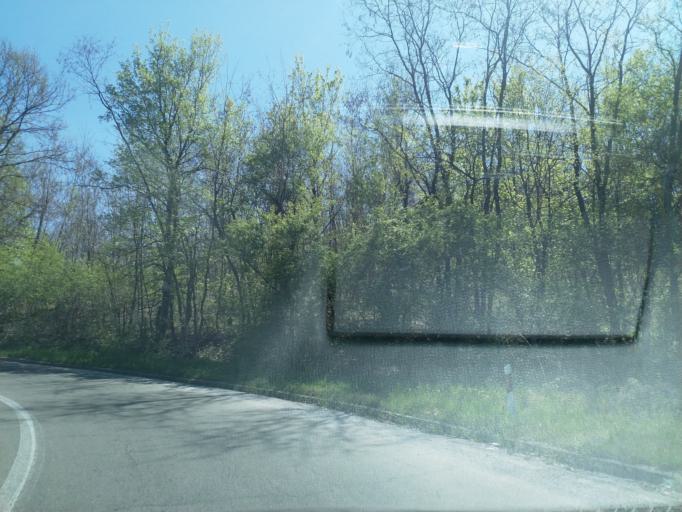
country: RS
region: Central Serbia
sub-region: Belgrade
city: Lazarevac
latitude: 44.3660
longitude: 20.3388
